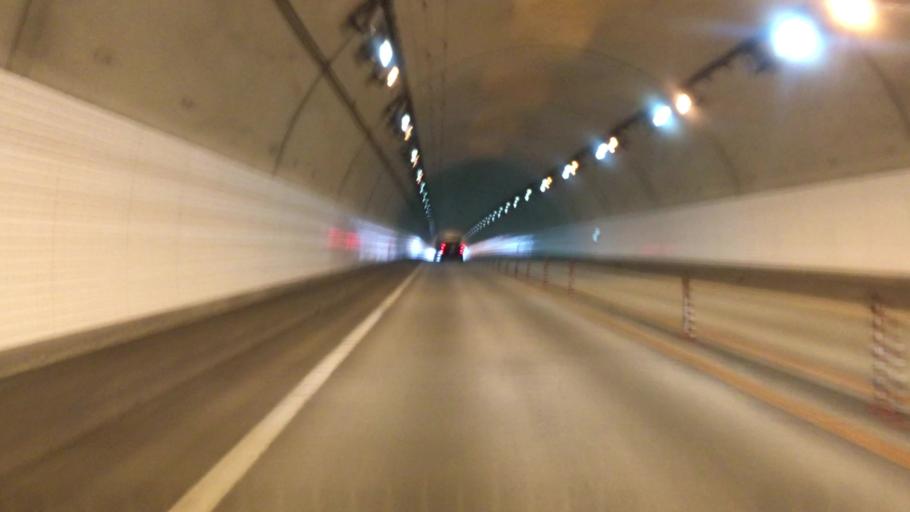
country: JP
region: Kyoto
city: Fukuchiyama
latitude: 35.2762
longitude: 134.9912
